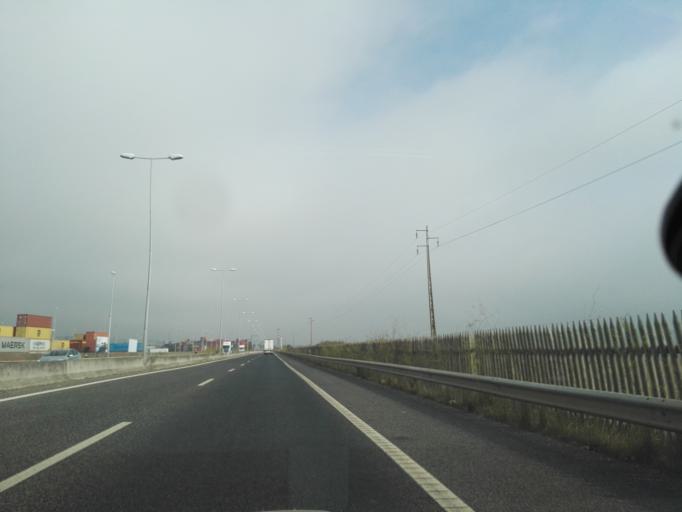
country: PT
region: Lisbon
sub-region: Loures
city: Sao Joao da Talha
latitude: 38.8121
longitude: -9.0888
